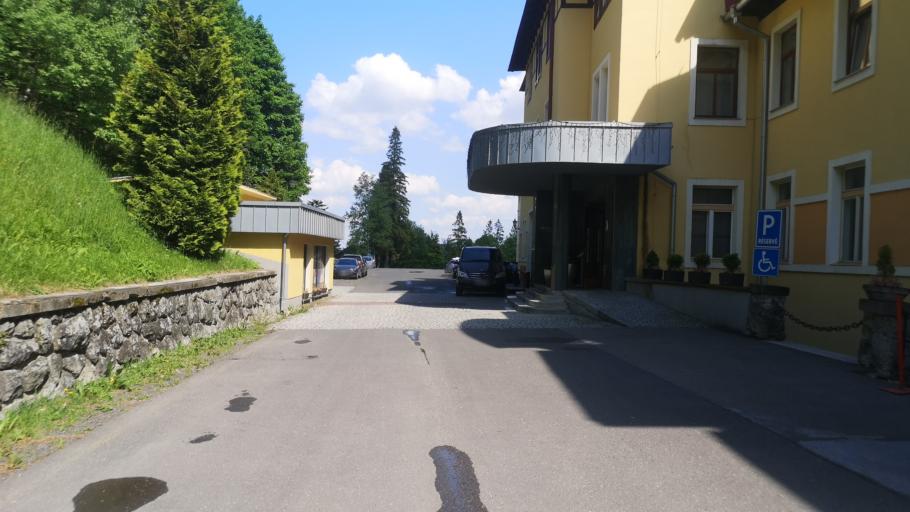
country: SK
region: Presovsky
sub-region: Okres Poprad
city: Nova Lesna
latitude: 49.1699
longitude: 20.2798
